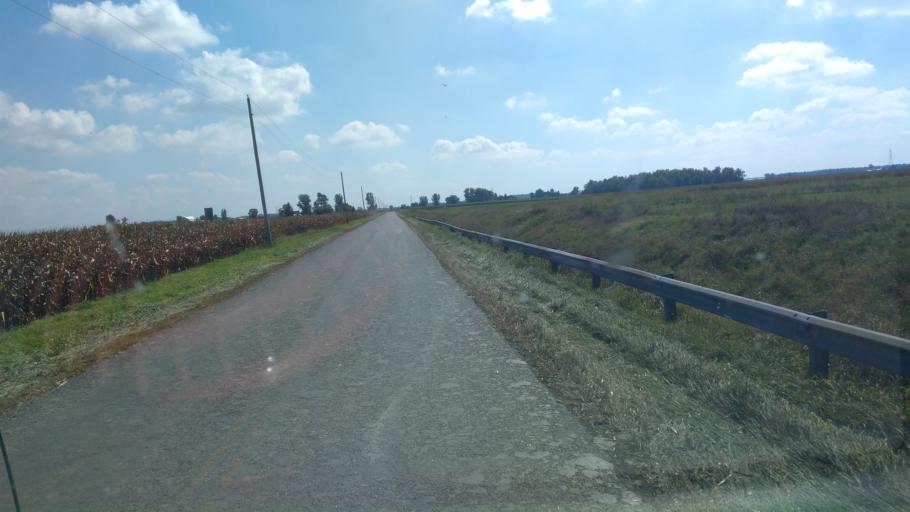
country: US
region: Ohio
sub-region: Hardin County
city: Ada
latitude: 40.6884
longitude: -83.8421
